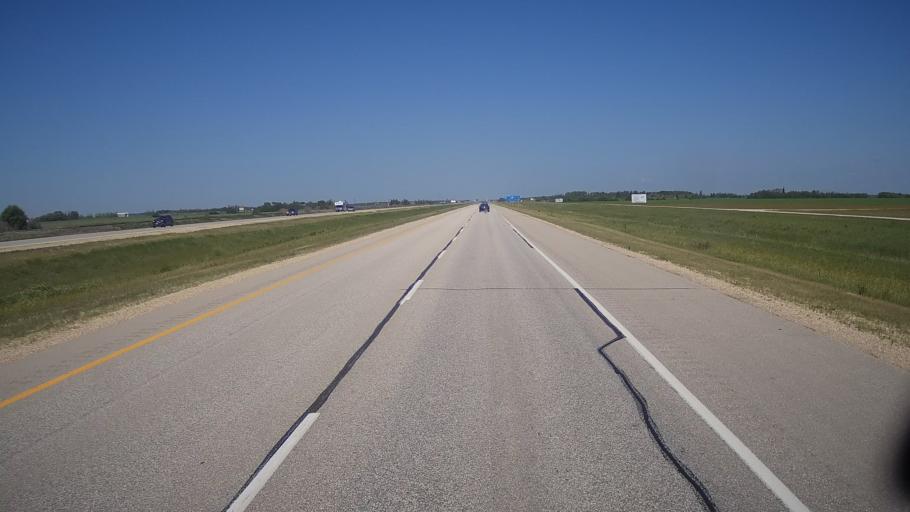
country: CA
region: Manitoba
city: Niverville
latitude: 49.8024
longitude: -96.8925
